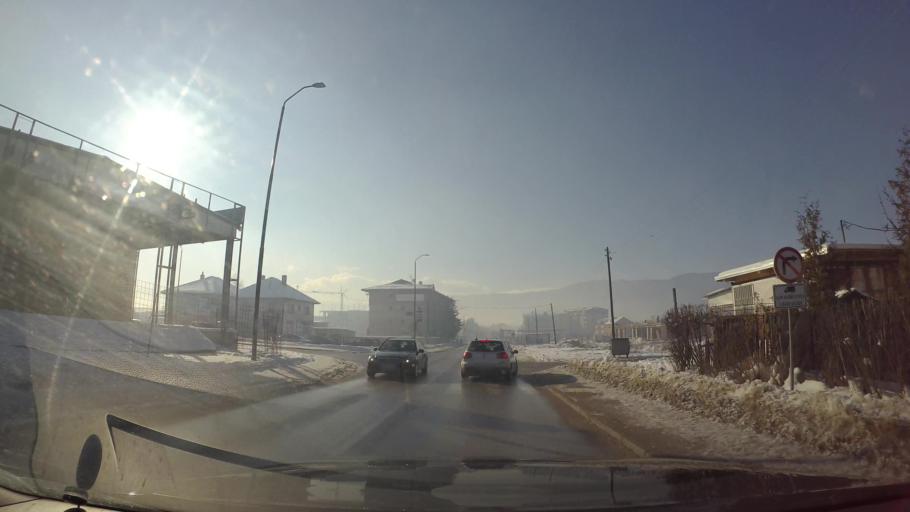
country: BA
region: Federation of Bosnia and Herzegovina
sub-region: Kanton Sarajevo
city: Sarajevo
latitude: 43.8193
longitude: 18.3566
